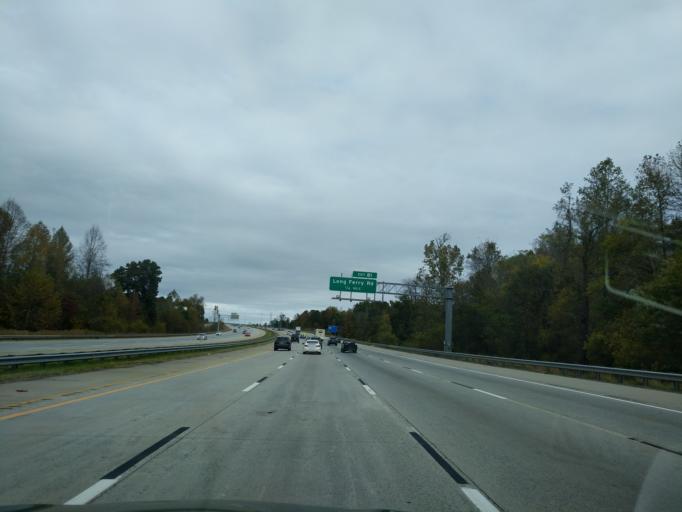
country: US
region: North Carolina
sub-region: Rowan County
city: East Spencer
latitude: 35.6855
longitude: -80.4054
